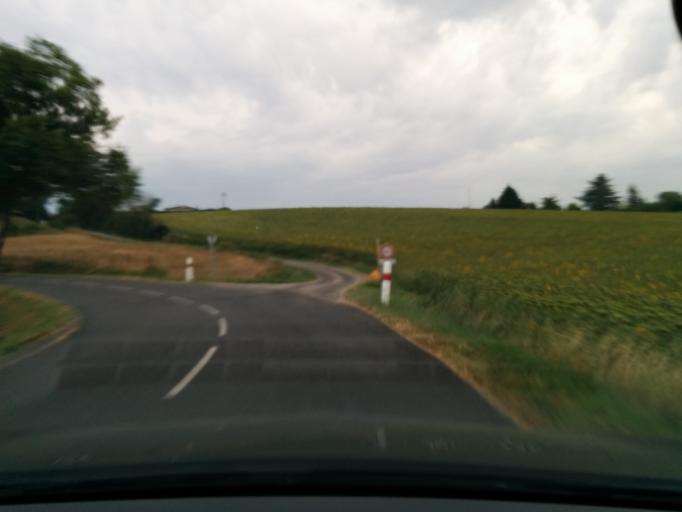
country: FR
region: Midi-Pyrenees
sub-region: Departement de la Haute-Garonne
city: Venerque
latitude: 43.4749
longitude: 1.4501
